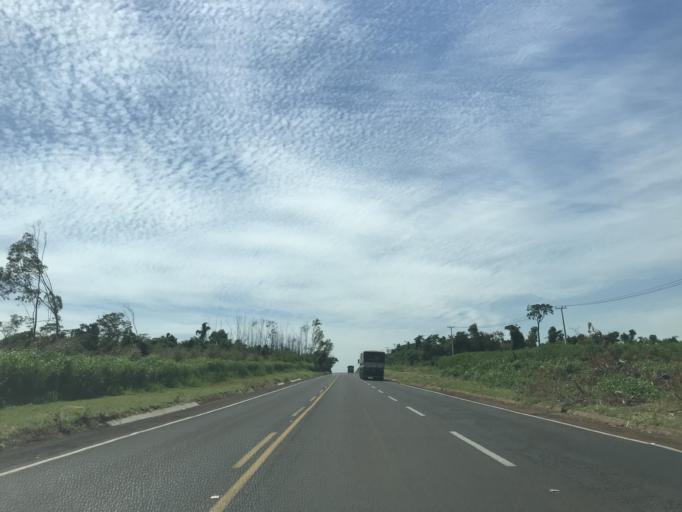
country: BR
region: Parana
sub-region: Paranavai
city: Nova Aurora
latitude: -22.9616
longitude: -52.6463
